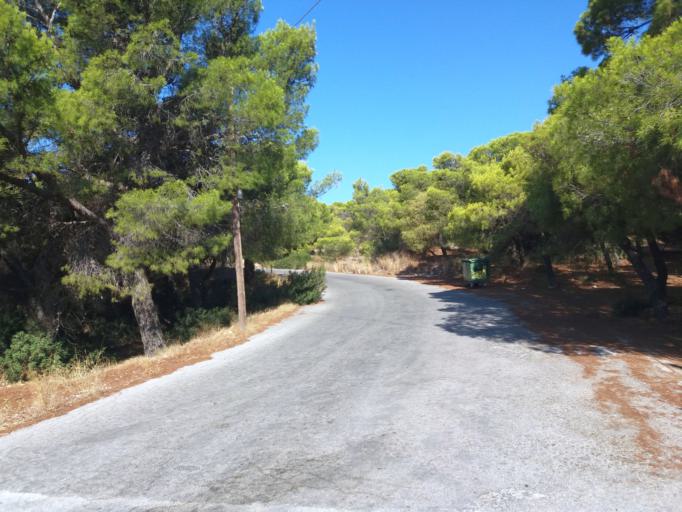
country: GR
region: Attica
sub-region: Nomos Piraios
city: Vathi
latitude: 37.7532
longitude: 23.5371
